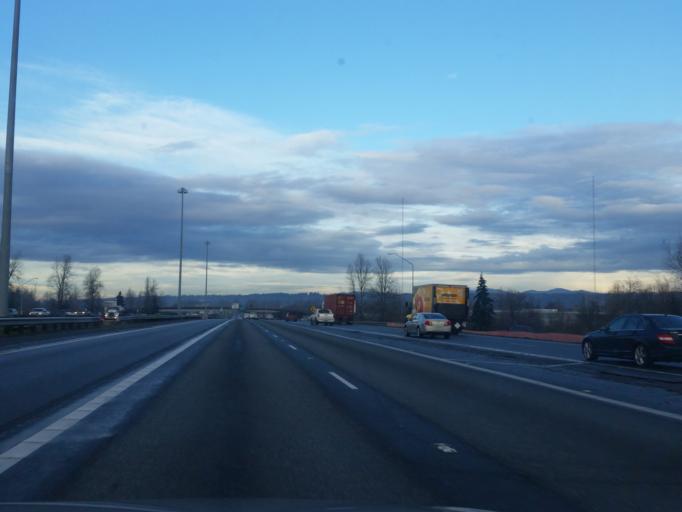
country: US
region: Washington
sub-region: King County
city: Auburn
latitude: 47.3035
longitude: -122.2517
